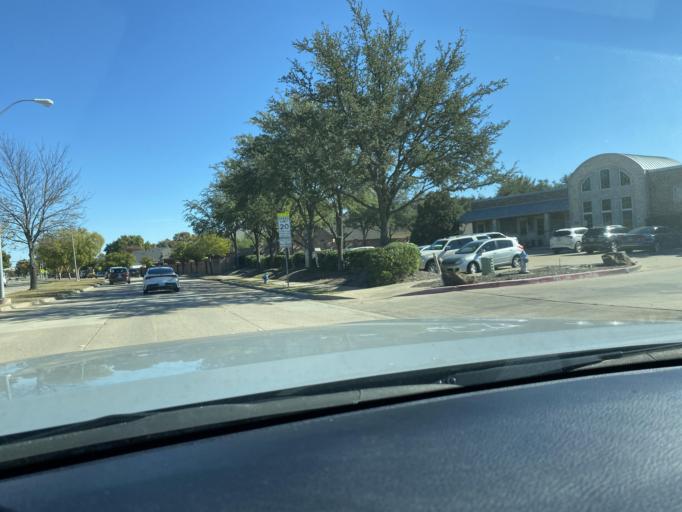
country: US
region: Texas
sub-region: Denton County
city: The Colony
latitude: 33.0452
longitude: -96.8246
